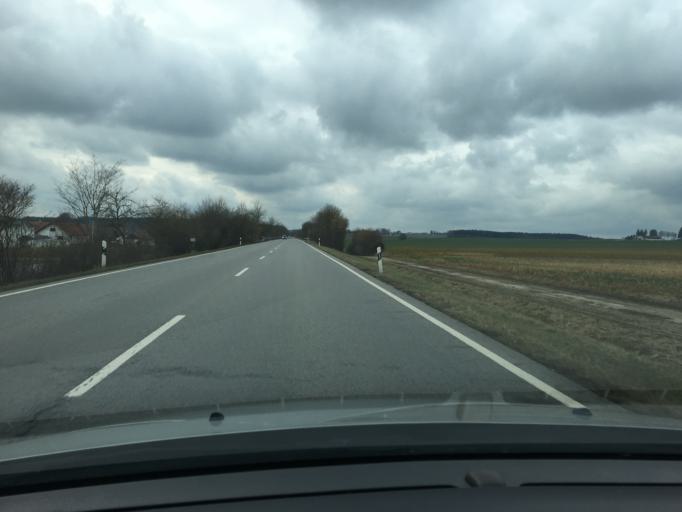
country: DE
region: Bavaria
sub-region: Upper Bavaria
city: Egglkofen
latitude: 48.4456
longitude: 12.4433
